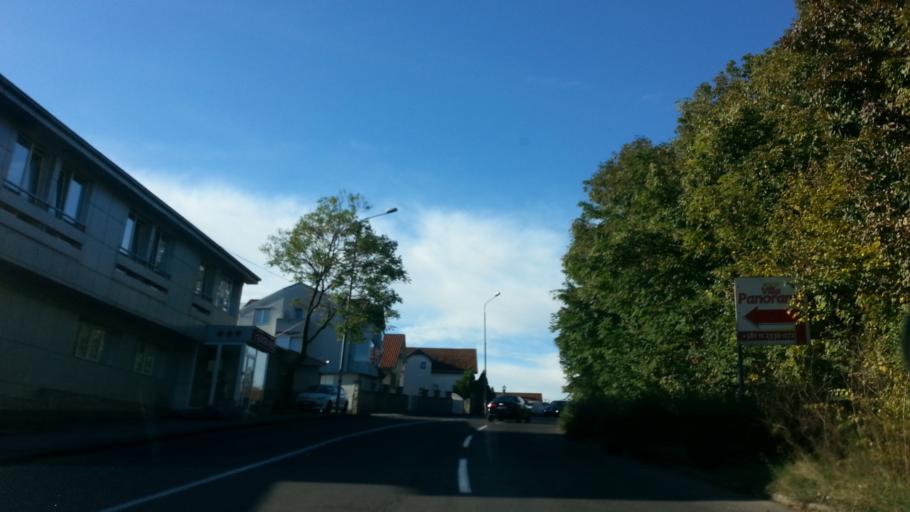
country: RS
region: Central Serbia
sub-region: Belgrade
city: Rakovica
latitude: 44.7433
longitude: 20.4301
